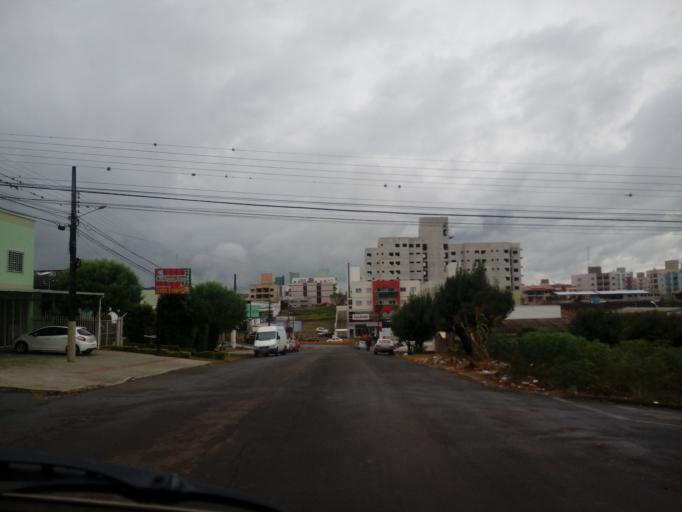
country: BR
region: Santa Catarina
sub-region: Chapeco
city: Chapeco
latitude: -27.0970
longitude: -52.6718
